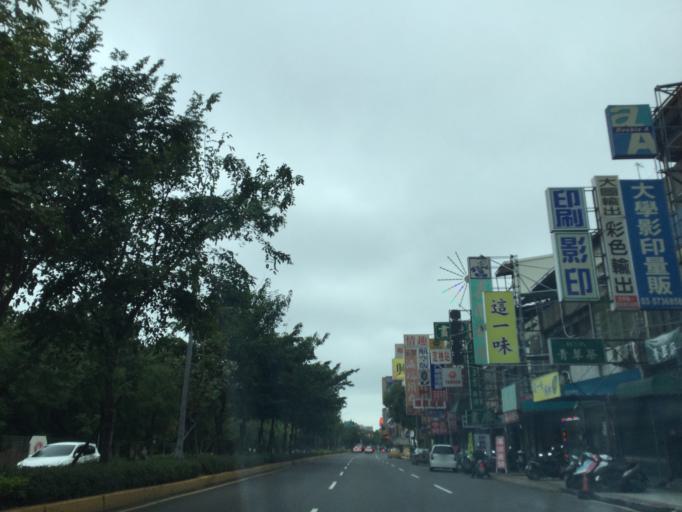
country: TW
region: Taiwan
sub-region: Hsinchu
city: Hsinchu
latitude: 24.7919
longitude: 121.0035
